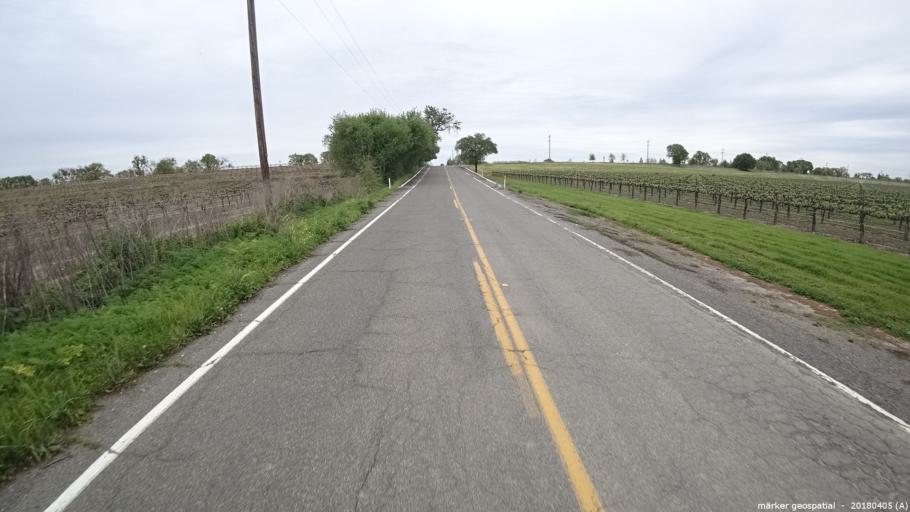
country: US
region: California
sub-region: Sacramento County
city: Walnut Grove
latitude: 38.3206
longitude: -121.5216
